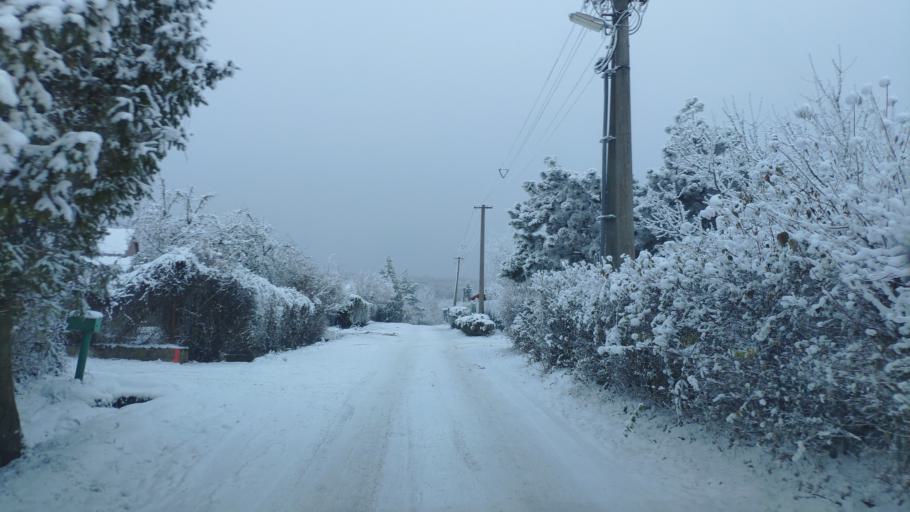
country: SK
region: Kosicky
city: Kosice
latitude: 48.6428
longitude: 21.1961
